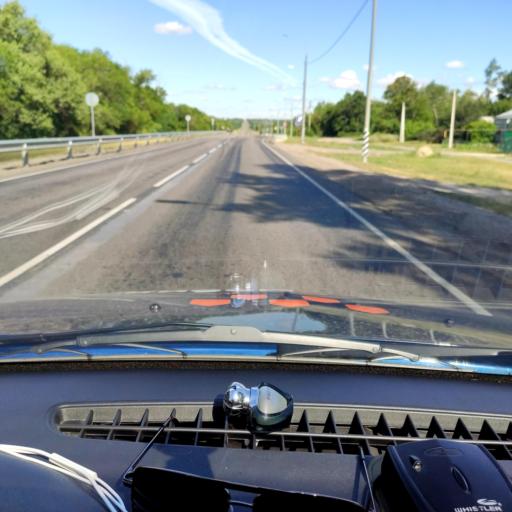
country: RU
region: Lipetsk
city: Khlevnoye
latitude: 52.1541
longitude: 39.1508
